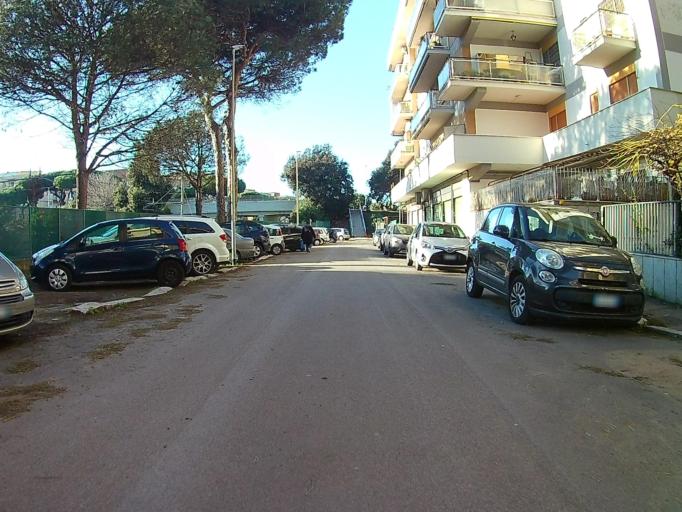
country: IT
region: Latium
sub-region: Citta metropolitana di Roma Capitale
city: Lido di Ostia
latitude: 41.7322
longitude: 12.2867
